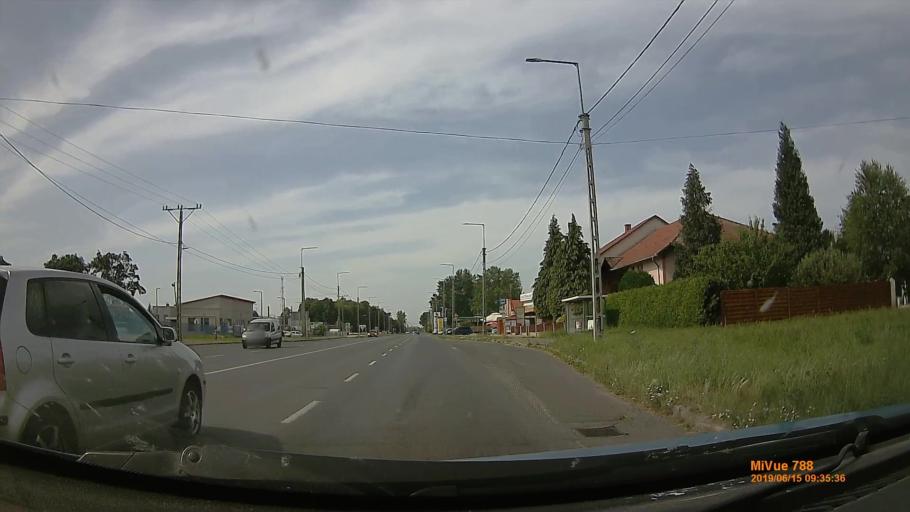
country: HU
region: Tolna
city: Dombovar
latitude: 46.3950
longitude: 18.1471
